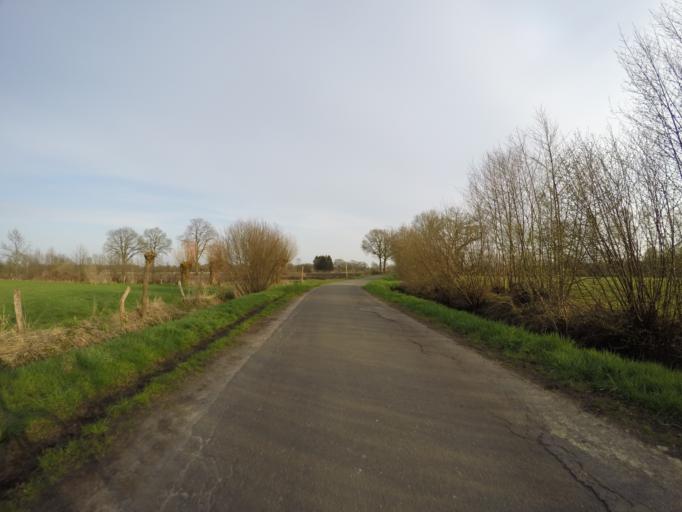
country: DE
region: Schleswig-Holstein
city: Bilsen
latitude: 53.7458
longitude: 9.8752
